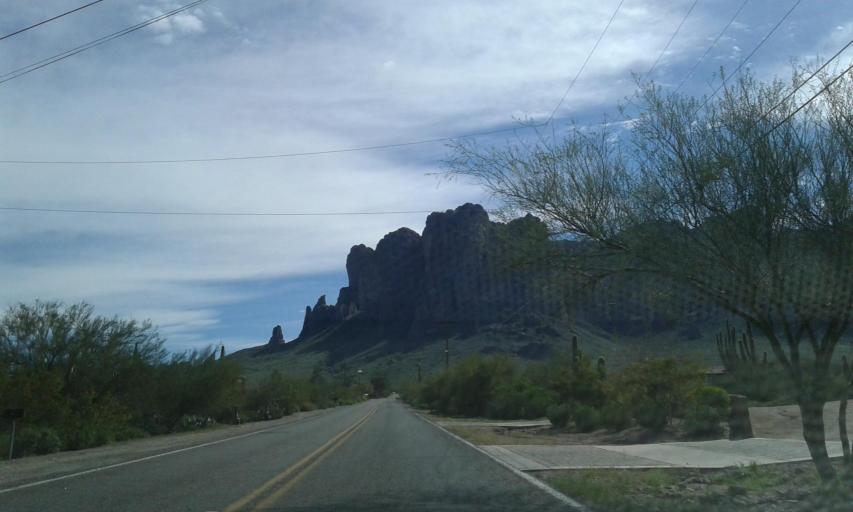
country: US
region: Arizona
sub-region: Pinal County
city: Apache Junction
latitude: 33.4496
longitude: -111.4847
